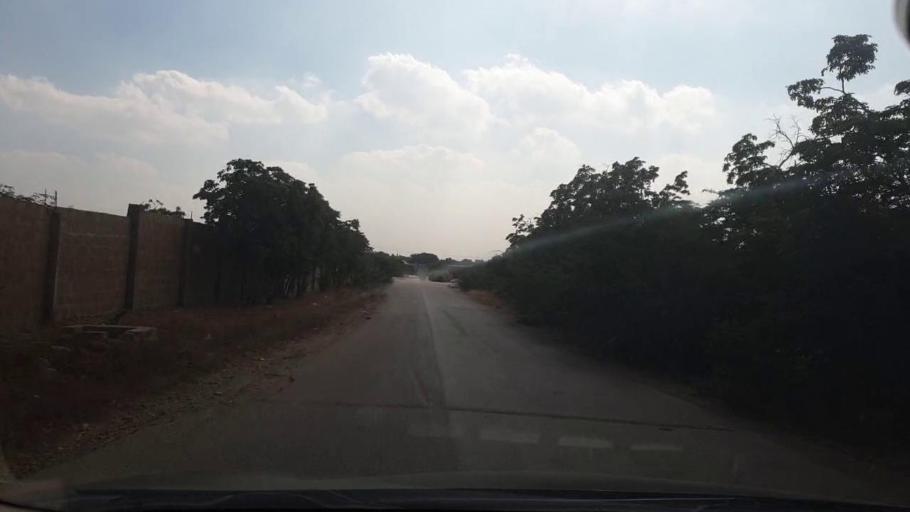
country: PK
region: Sindh
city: Malir Cantonment
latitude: 25.0090
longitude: 67.3555
